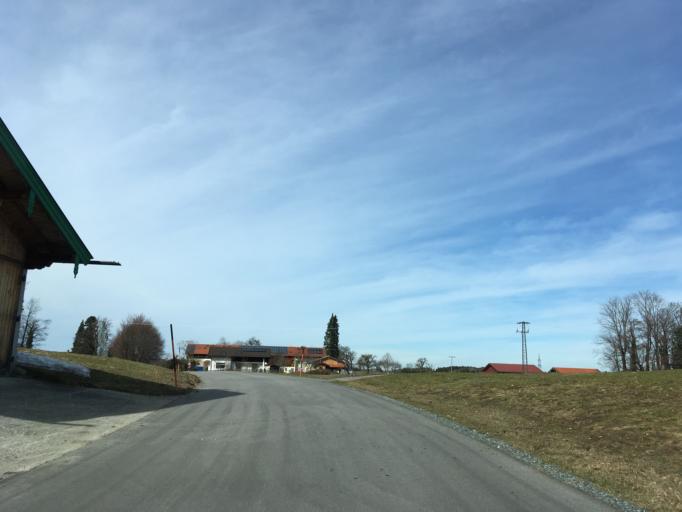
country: DE
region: Bavaria
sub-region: Upper Bavaria
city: Aschau im Chiemgau
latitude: 47.8001
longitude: 12.3423
